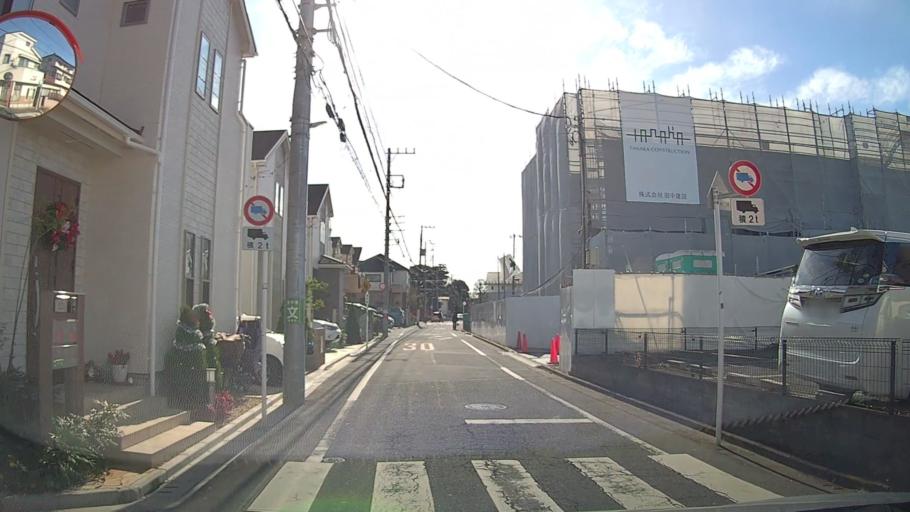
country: JP
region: Saitama
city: Wako
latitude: 35.7560
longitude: 139.6168
